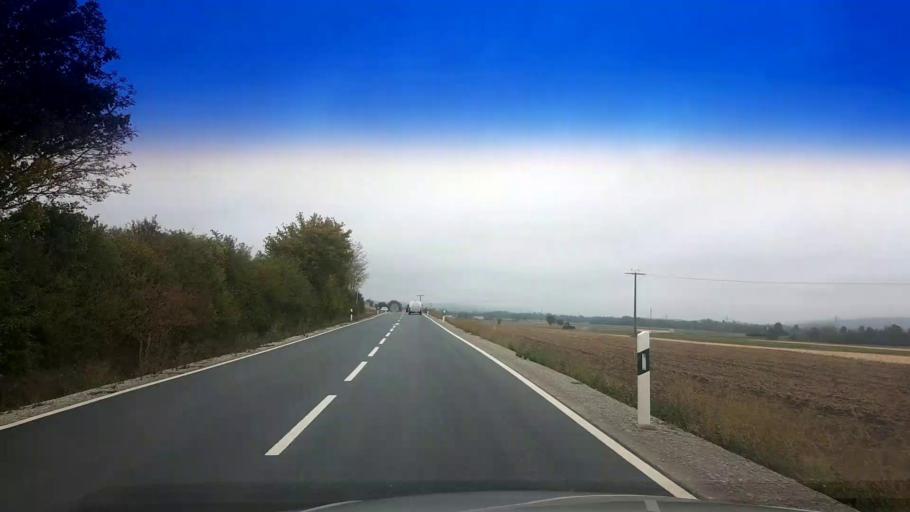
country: DE
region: Bavaria
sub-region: Upper Franconia
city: Buttenheim
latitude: 49.7903
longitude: 11.0391
